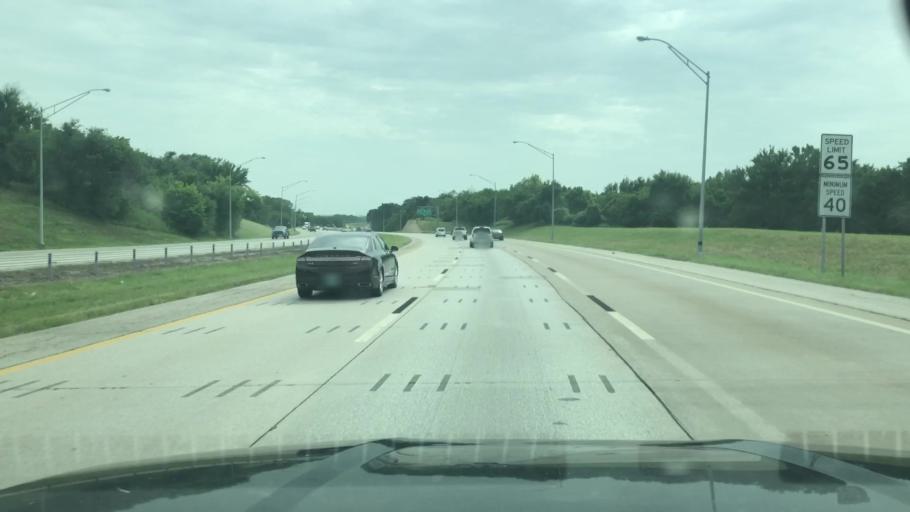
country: US
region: Oklahoma
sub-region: Tulsa County
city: Sand Springs
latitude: 36.1576
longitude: -96.0559
